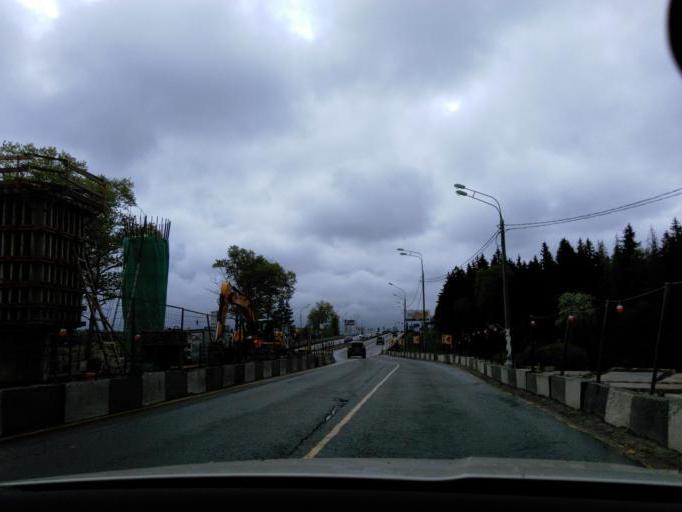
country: RU
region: Moskovskaya
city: Rzhavki
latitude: 55.9935
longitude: 37.2603
